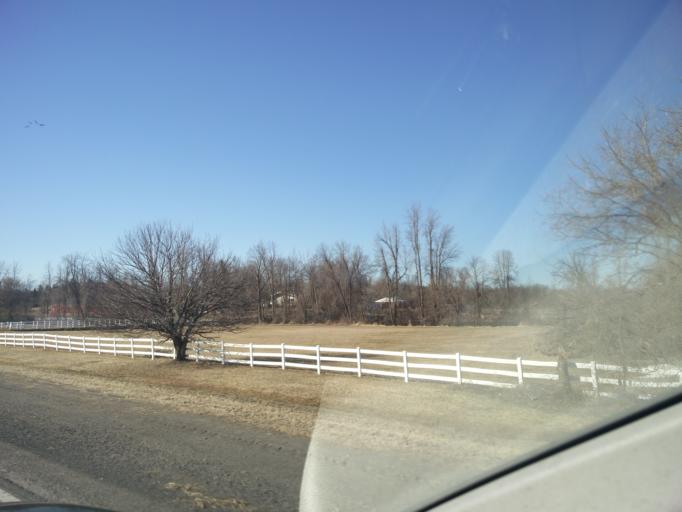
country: CA
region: Ontario
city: Bells Corners
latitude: 45.1602
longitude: -75.7088
